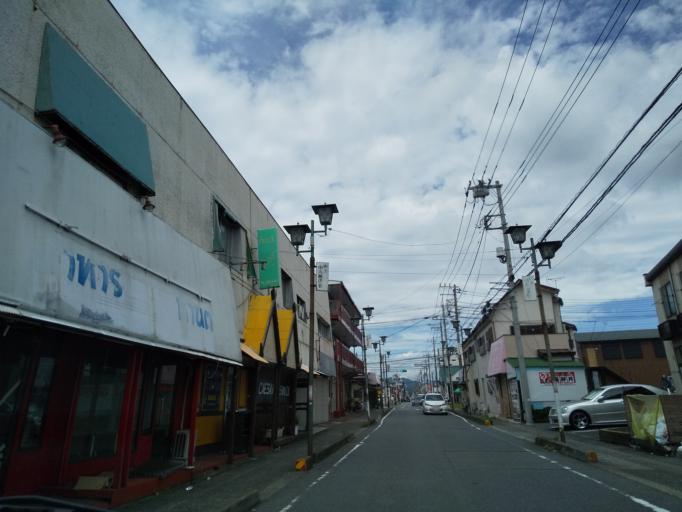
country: JP
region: Kanagawa
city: Zama
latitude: 35.5140
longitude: 139.3389
